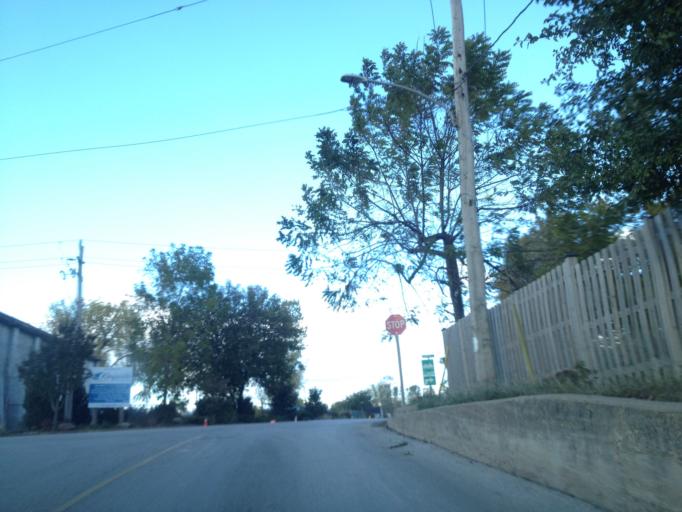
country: CA
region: Ontario
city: Amherstburg
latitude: 42.0283
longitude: -82.7328
